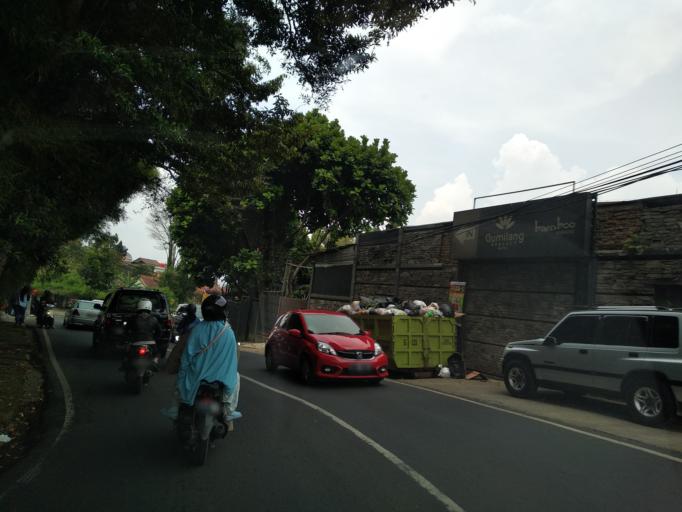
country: ID
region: West Java
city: Lembang
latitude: -6.8455
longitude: 107.5995
